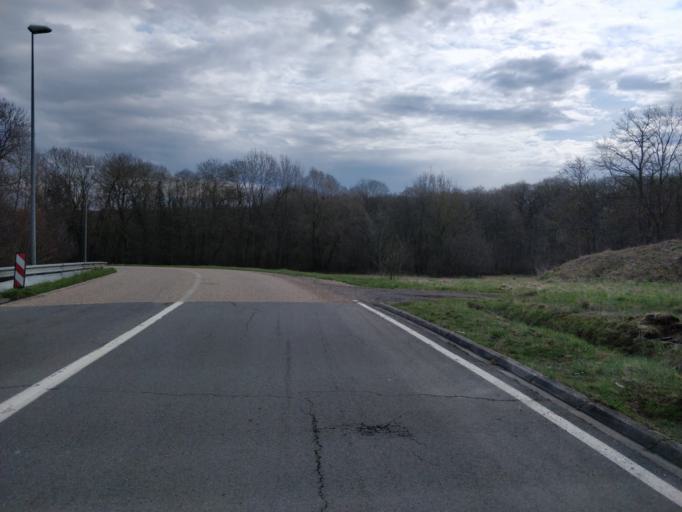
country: FR
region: Lorraine
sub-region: Departement de la Moselle
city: Gandrange
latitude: 49.2831
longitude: 6.1264
